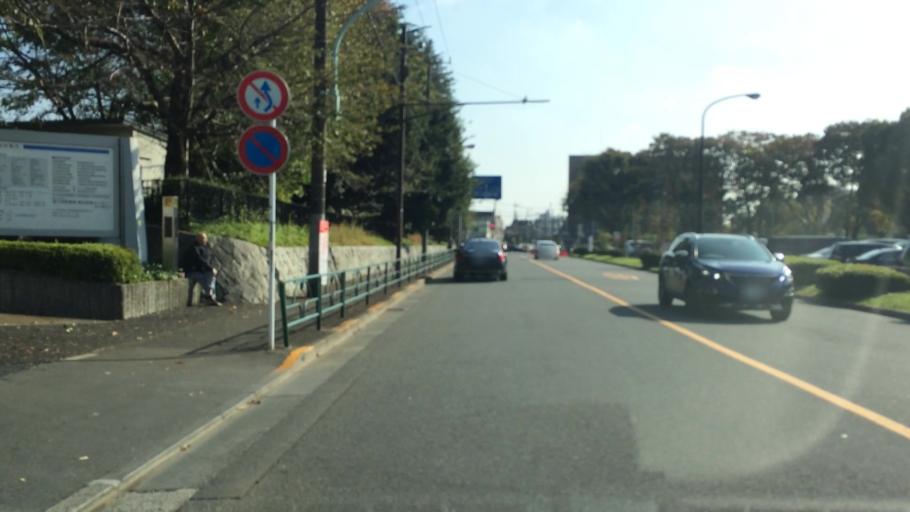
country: JP
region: Tokyo
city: Tokyo
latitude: 35.6262
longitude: 139.6652
